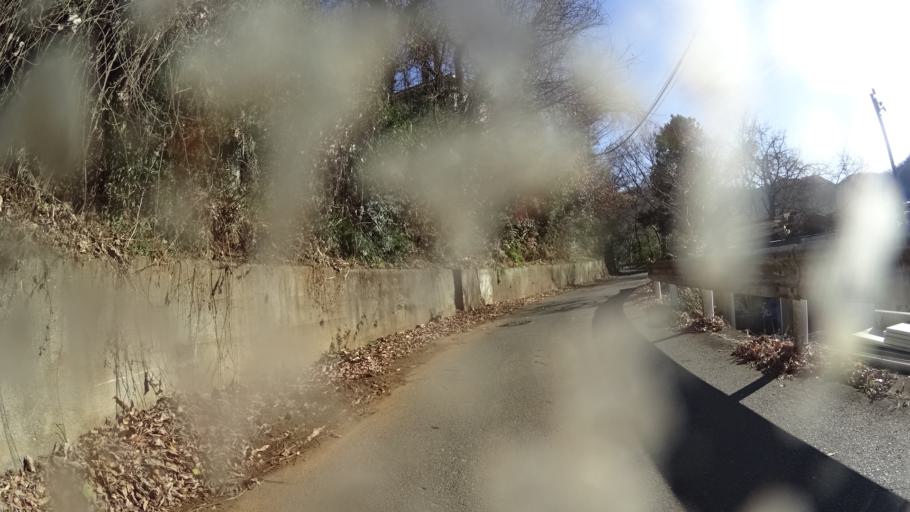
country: JP
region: Yamanashi
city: Uenohara
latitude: 35.6164
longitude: 139.1651
